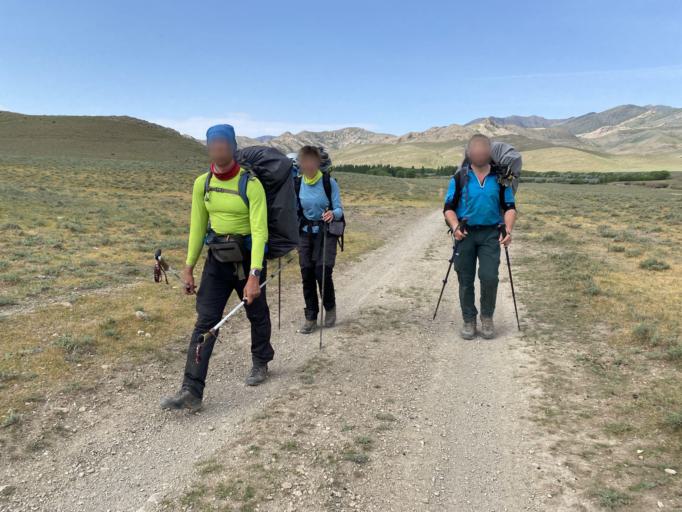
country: KZ
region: Ongtustik Qazaqstan
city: Kentau
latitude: 44.0266
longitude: 68.2290
